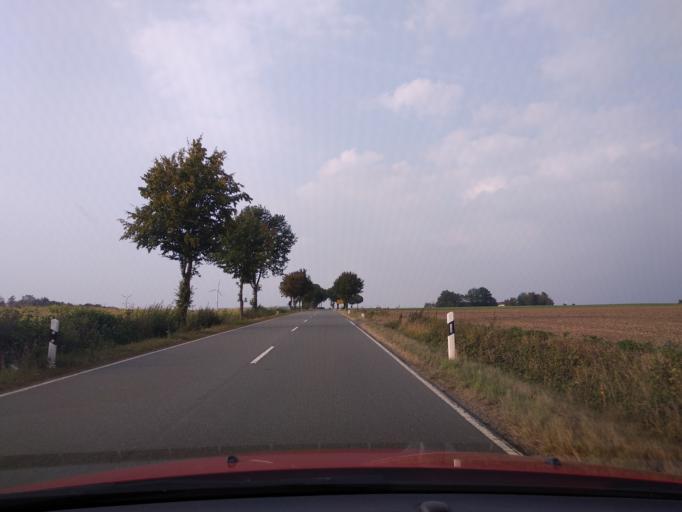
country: DE
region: North Rhine-Westphalia
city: Borgentreich
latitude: 51.5565
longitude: 9.2978
